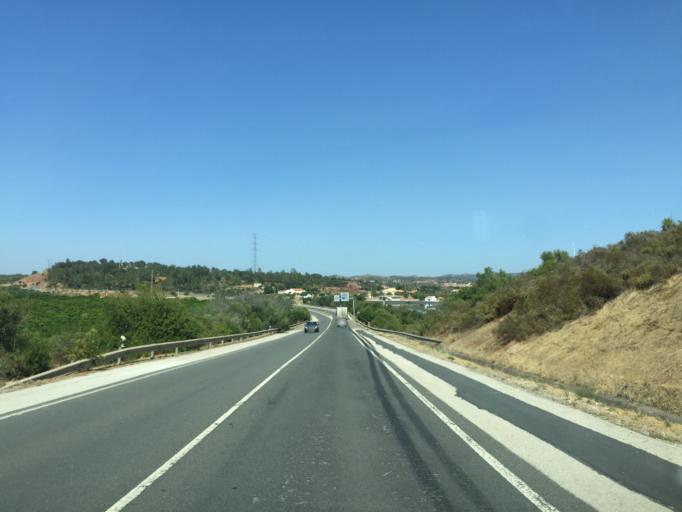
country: PT
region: Faro
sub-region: Silves
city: Sao Bartolomeu de Messines
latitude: 37.2459
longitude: -8.2752
